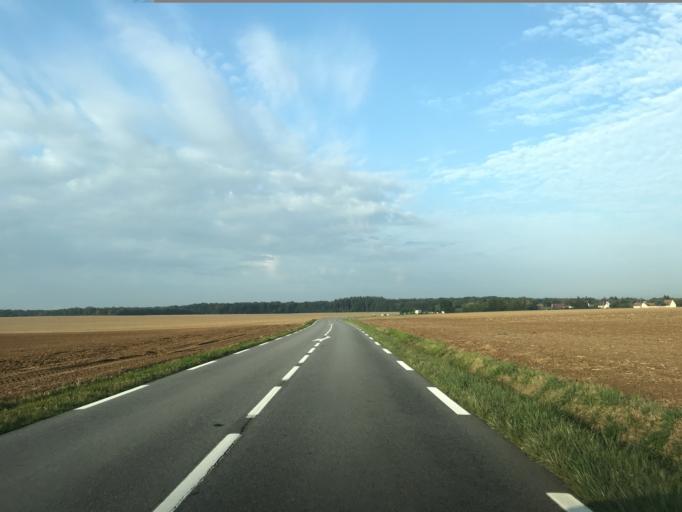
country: FR
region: Haute-Normandie
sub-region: Departement de l'Eure
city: Gravigny
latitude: 49.0677
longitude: 1.2109
